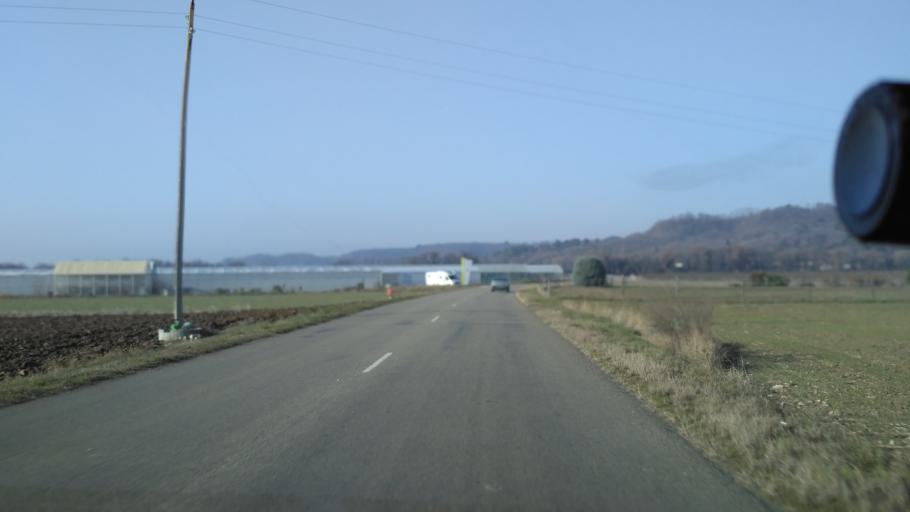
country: FR
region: Rhone-Alpes
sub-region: Departement de la Drome
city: Clerieux
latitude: 45.0582
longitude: 5.0012
